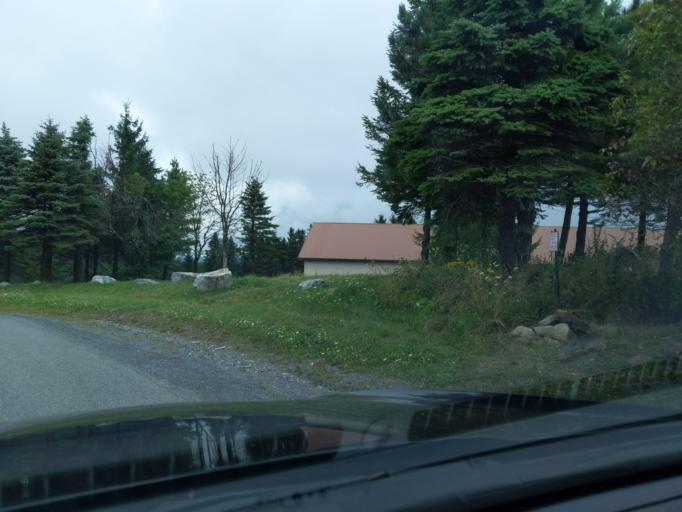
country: US
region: Pennsylvania
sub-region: Blair County
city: Claysburg
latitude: 40.2889
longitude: -78.5639
